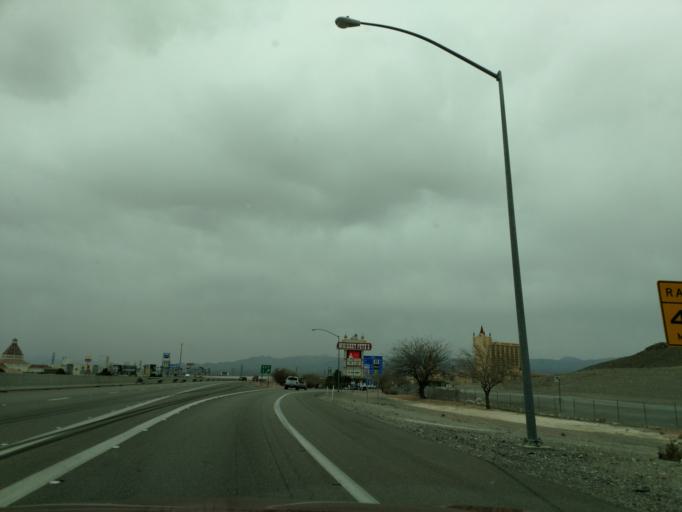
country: US
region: Nevada
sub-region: Clark County
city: Sandy Valley
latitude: 35.6157
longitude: -115.3880
